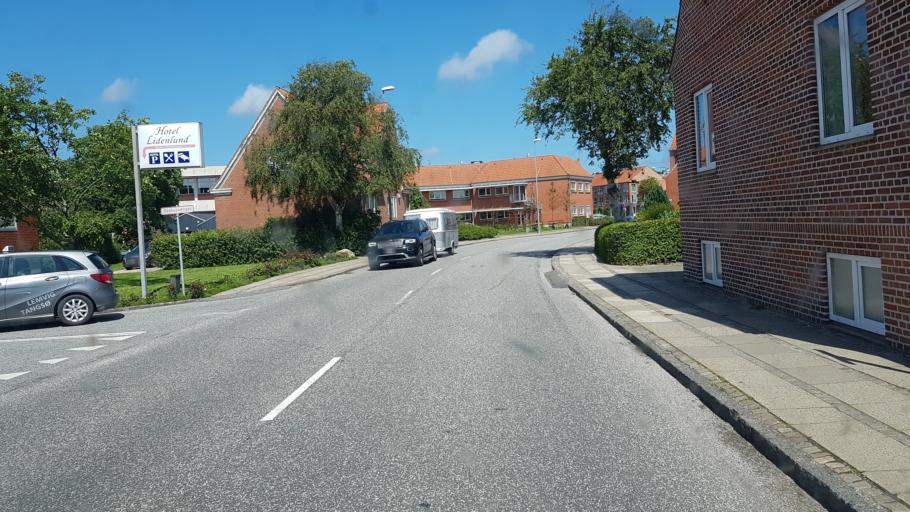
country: DK
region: Central Jutland
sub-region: Lemvig Kommune
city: Lemvig
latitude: 56.5488
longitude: 8.3127
